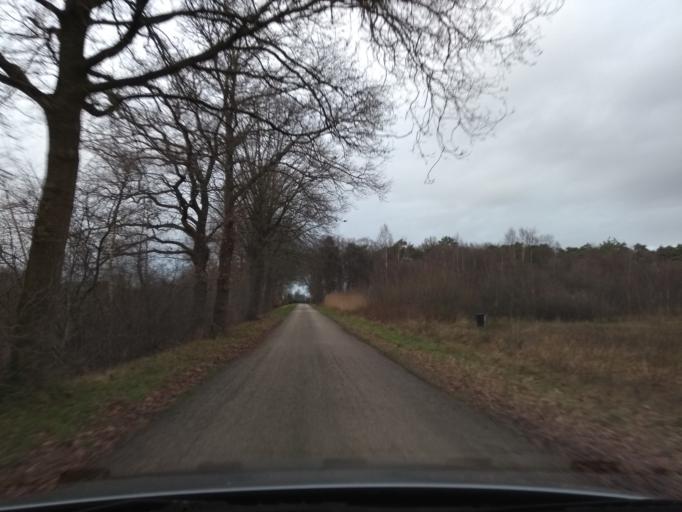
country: NL
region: Overijssel
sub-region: Gemeente Haaksbergen
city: Haaksbergen
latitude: 52.1257
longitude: 6.7586
